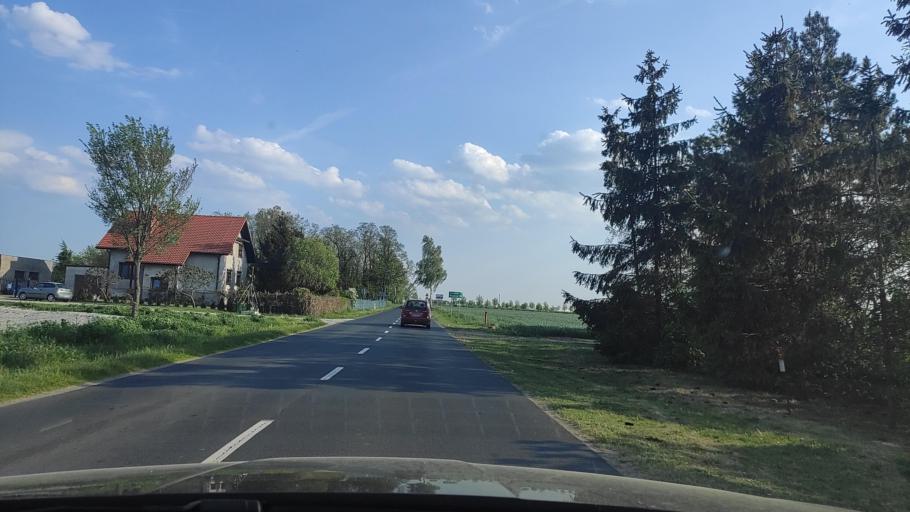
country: PL
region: Greater Poland Voivodeship
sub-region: Powiat poznanski
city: Kleszczewo
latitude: 52.3480
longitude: 17.1711
